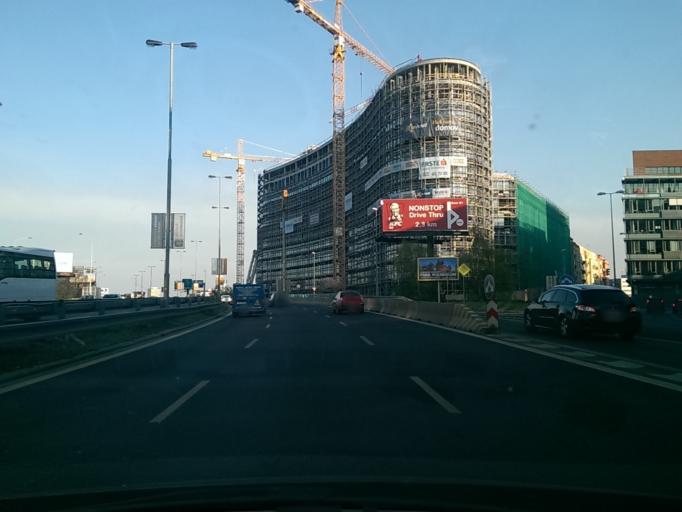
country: CZ
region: Praha
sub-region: Praha 2
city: Vysehrad
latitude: 50.0535
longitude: 14.4401
